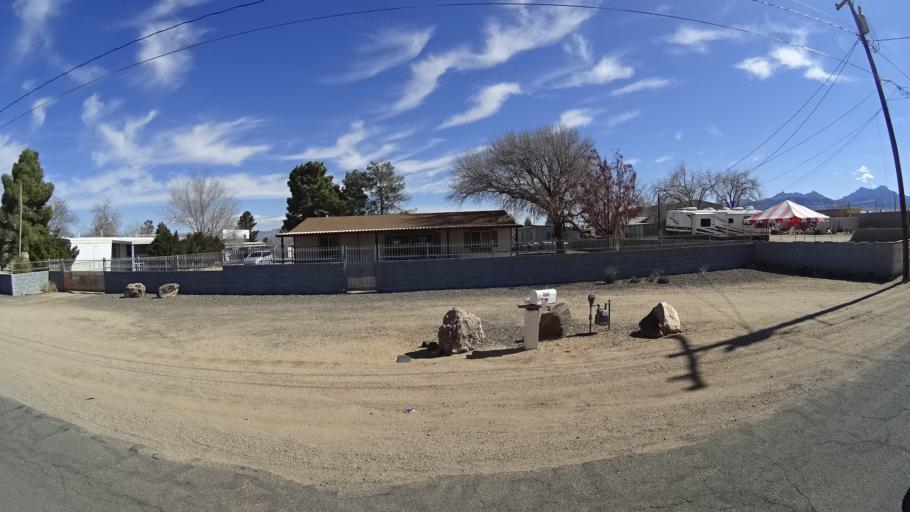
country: US
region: Arizona
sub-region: Mohave County
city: New Kingman-Butler
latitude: 35.2419
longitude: -114.0132
